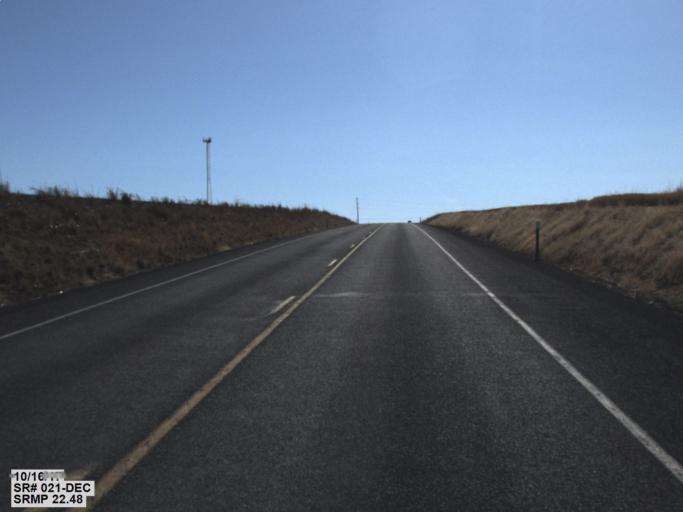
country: US
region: Washington
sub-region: Adams County
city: Ritzville
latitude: 46.9456
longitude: -118.5657
